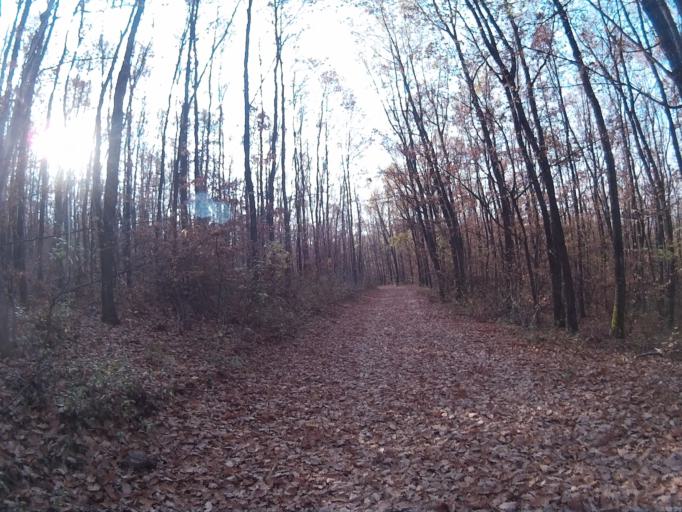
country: HU
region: Heves
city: Belapatfalva
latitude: 48.0053
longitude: 20.3836
